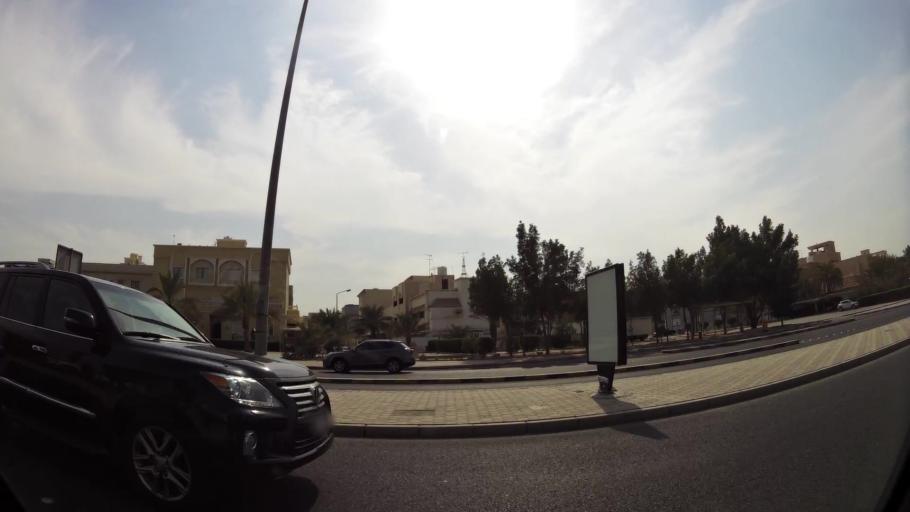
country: KW
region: Al Asimah
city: Ash Shamiyah
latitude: 29.3450
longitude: 47.9642
